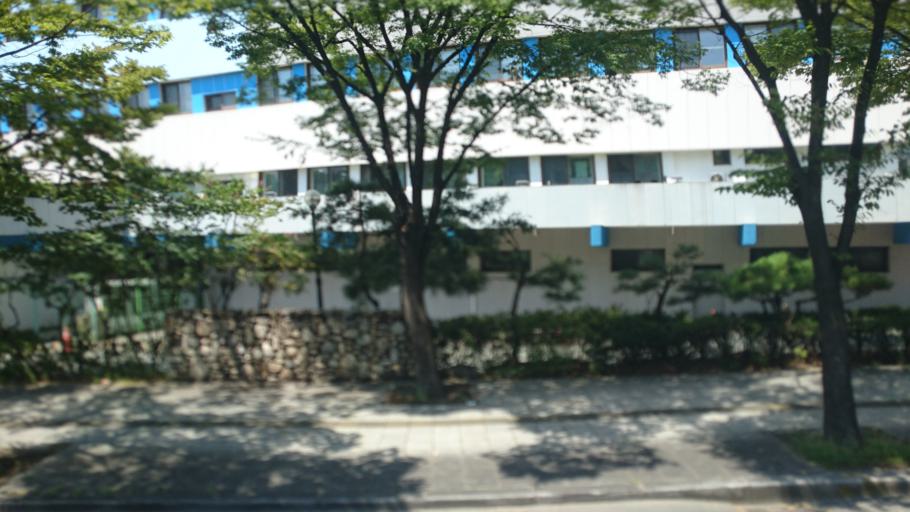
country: KR
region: Daegu
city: Daegu
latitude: 35.8839
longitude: 128.6249
